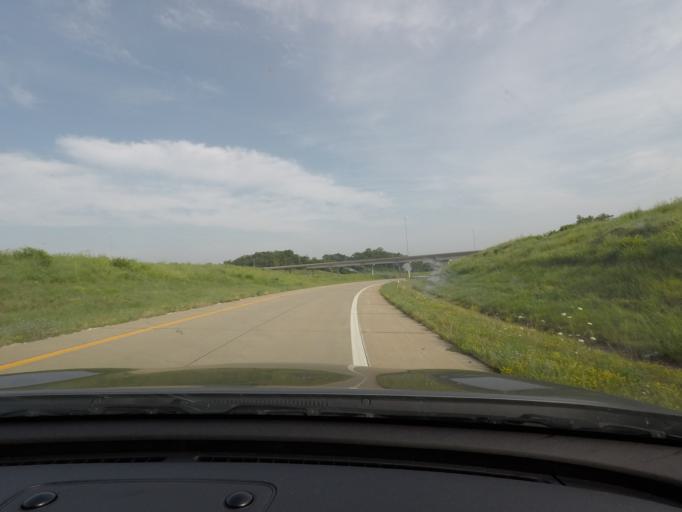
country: US
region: Missouri
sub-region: Saint Charles County
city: Saint Peters
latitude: 38.7993
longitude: -90.5887
